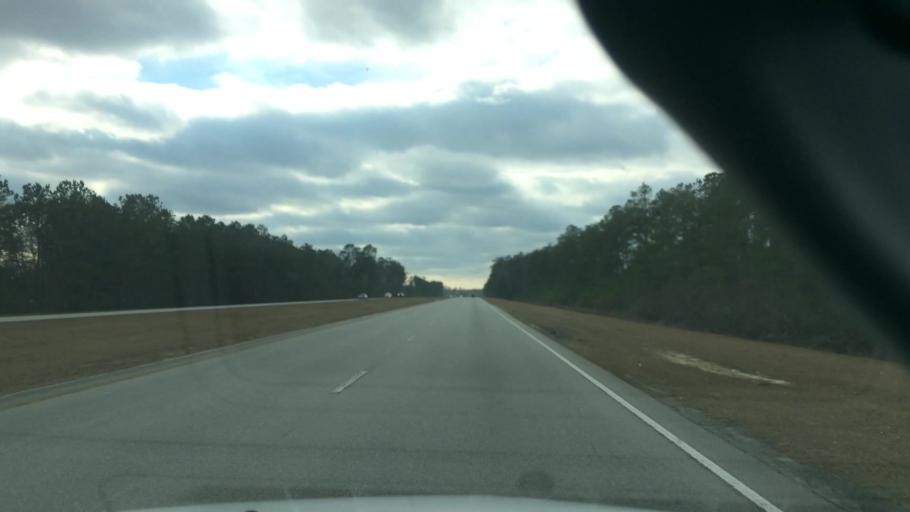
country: US
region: North Carolina
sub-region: Brunswick County
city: Bolivia
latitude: 34.0606
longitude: -78.2040
